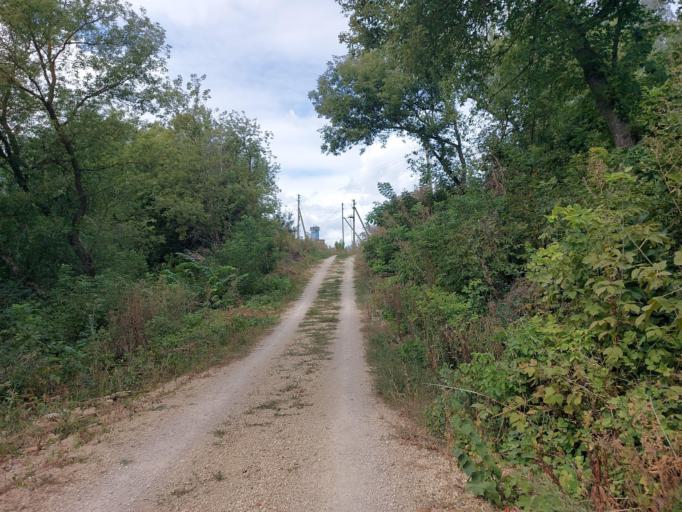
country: RU
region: Lipetsk
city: Terbuny
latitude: 52.2603
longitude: 38.2079
